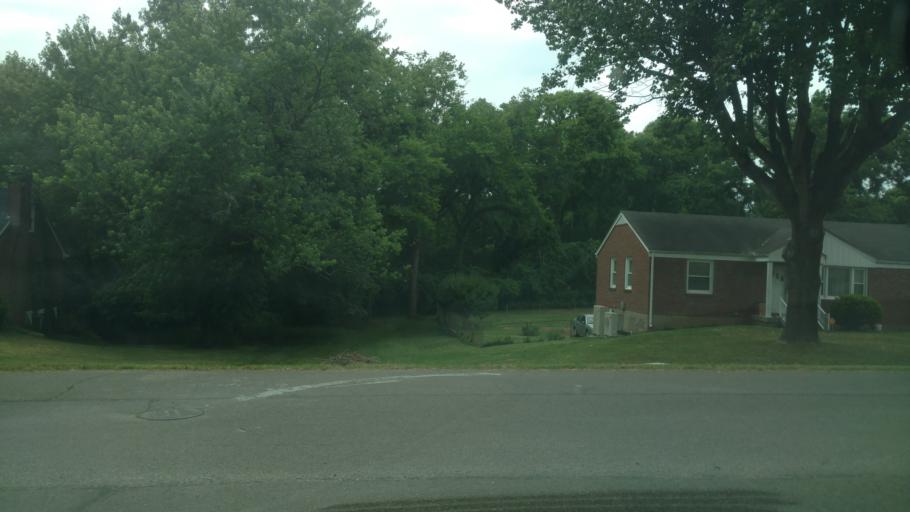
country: US
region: Tennessee
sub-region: Davidson County
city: Lakewood
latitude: 36.2042
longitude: -86.7042
